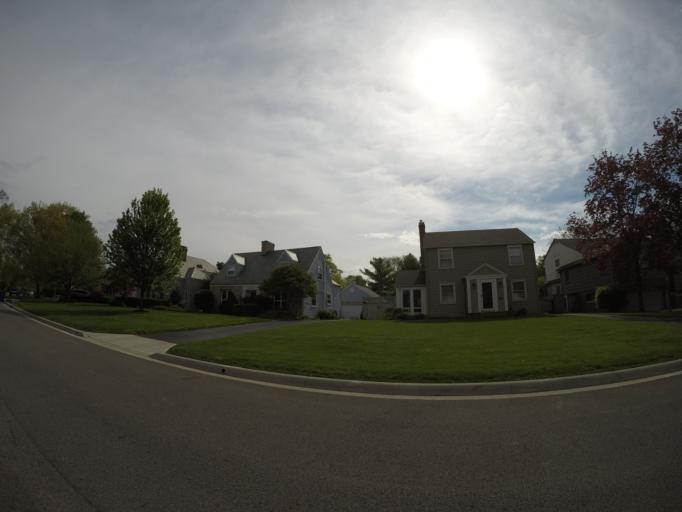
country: US
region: Ohio
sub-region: Franklin County
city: Upper Arlington
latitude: 39.9973
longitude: -83.0544
